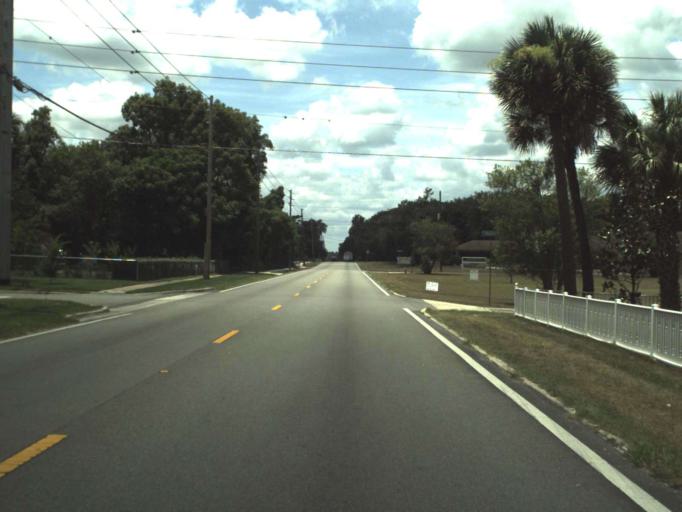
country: US
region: Florida
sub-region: Volusia County
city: West DeLand
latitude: 29.0279
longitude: -81.3285
